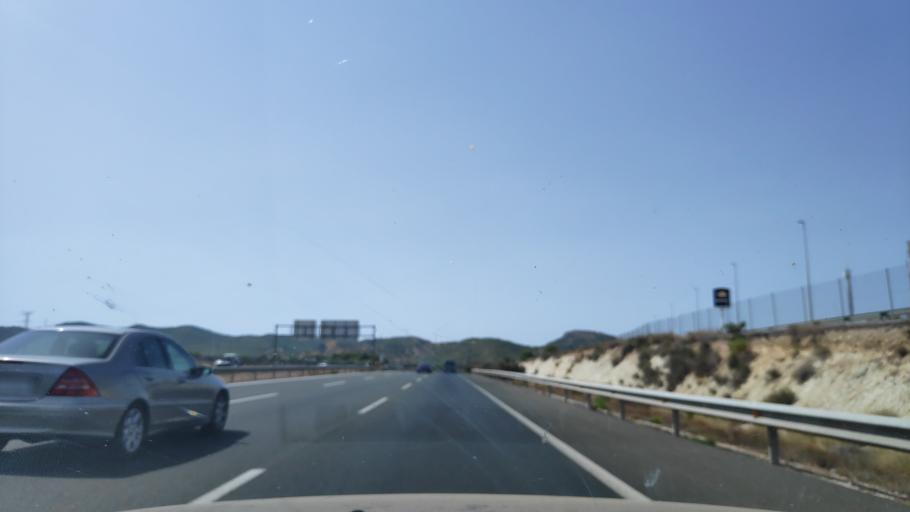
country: ES
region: Murcia
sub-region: Murcia
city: Murcia
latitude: 37.8828
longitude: -1.1349
